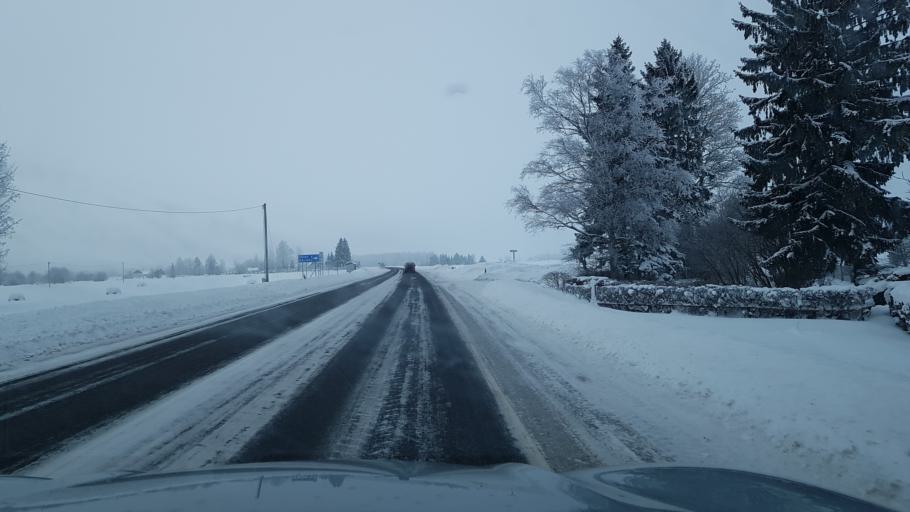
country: EE
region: Ida-Virumaa
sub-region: Johvi vald
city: Johvi
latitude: 59.2725
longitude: 27.3866
